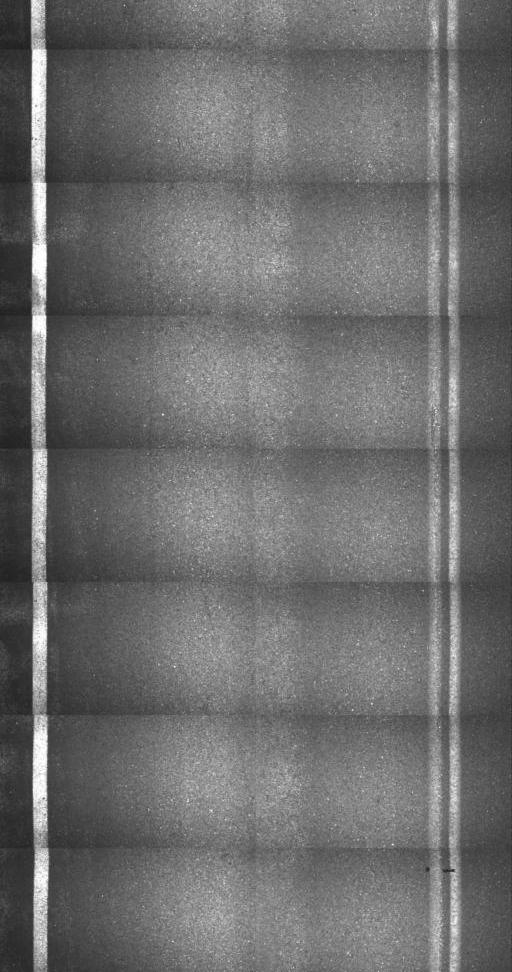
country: US
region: Vermont
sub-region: Caledonia County
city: Lyndonville
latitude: 44.6555
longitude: -72.1622
